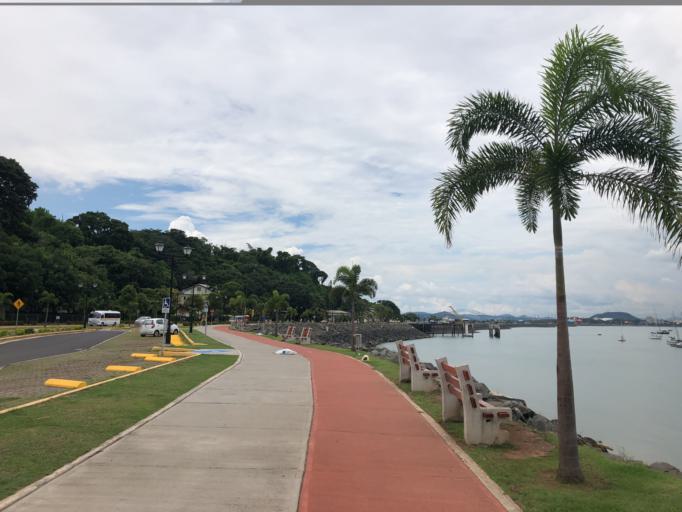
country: PA
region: Panama
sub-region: Distrito de Panama
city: Ancon
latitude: 8.9155
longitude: -79.5302
